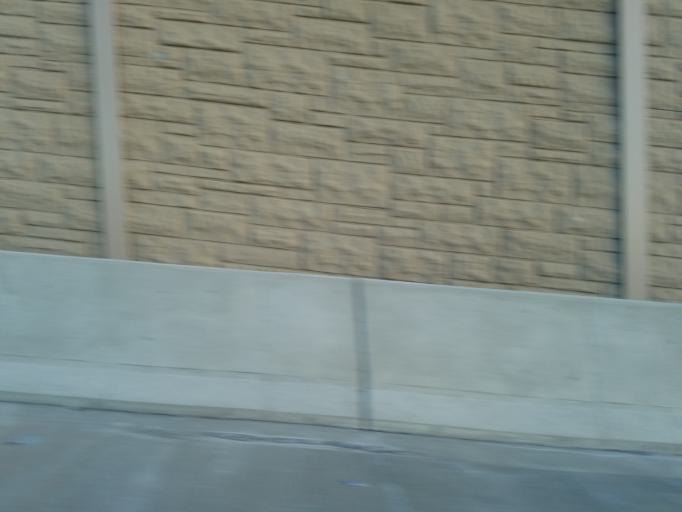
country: US
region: Illinois
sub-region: DuPage County
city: Itasca
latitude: 41.9822
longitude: -88.0199
